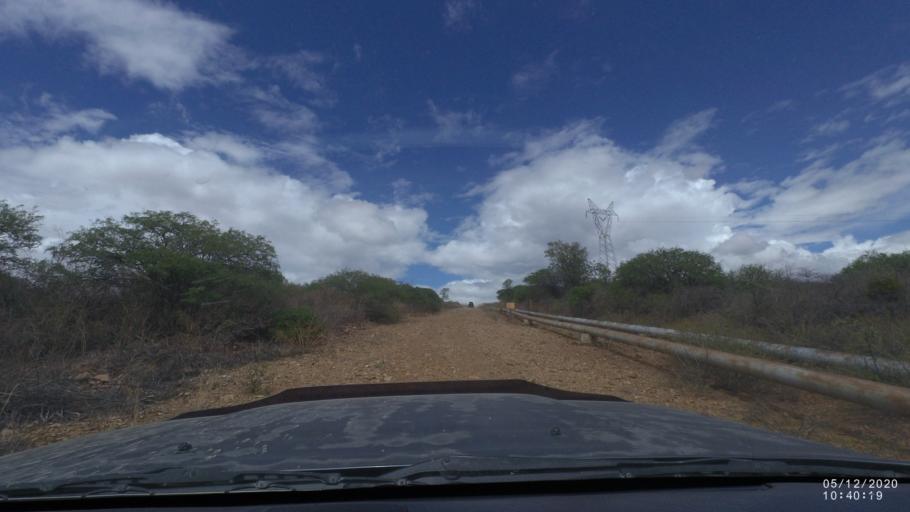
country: BO
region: Cochabamba
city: Sipe Sipe
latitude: -17.5456
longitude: -66.2864
